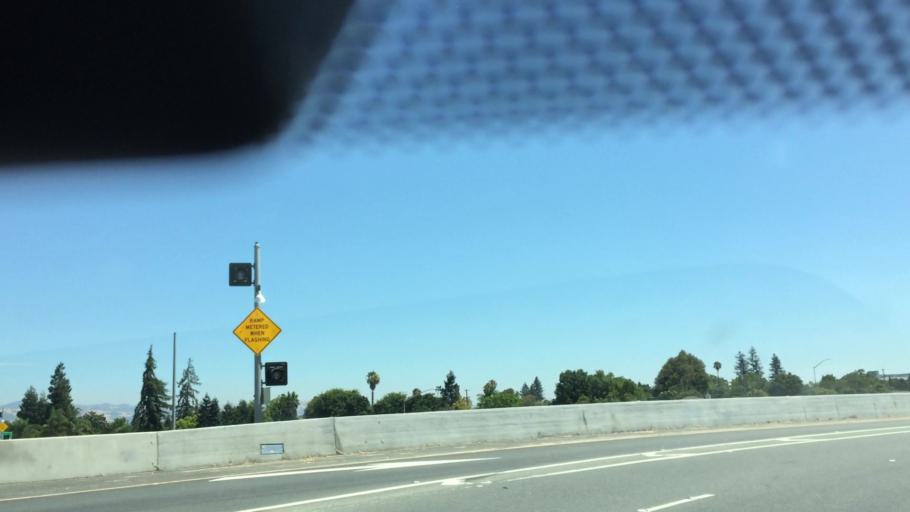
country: US
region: California
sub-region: Santa Clara County
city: Burbank
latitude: 37.3230
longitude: -121.9414
